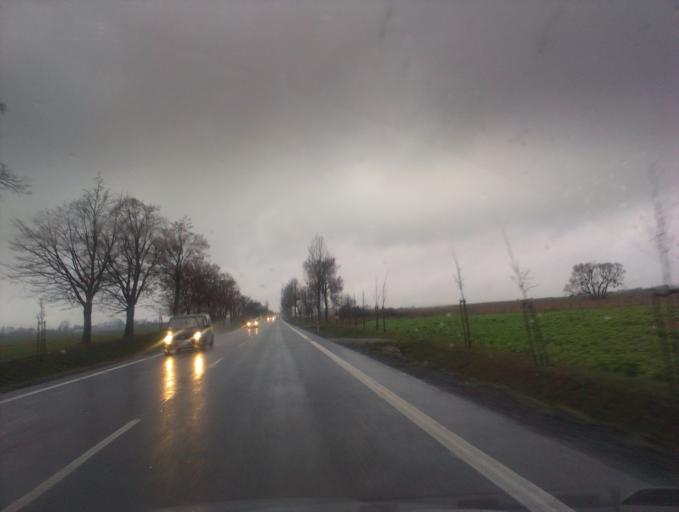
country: PL
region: Greater Poland Voivodeship
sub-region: Powiat obornicki
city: Oborniki
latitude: 52.6117
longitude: 16.8155
